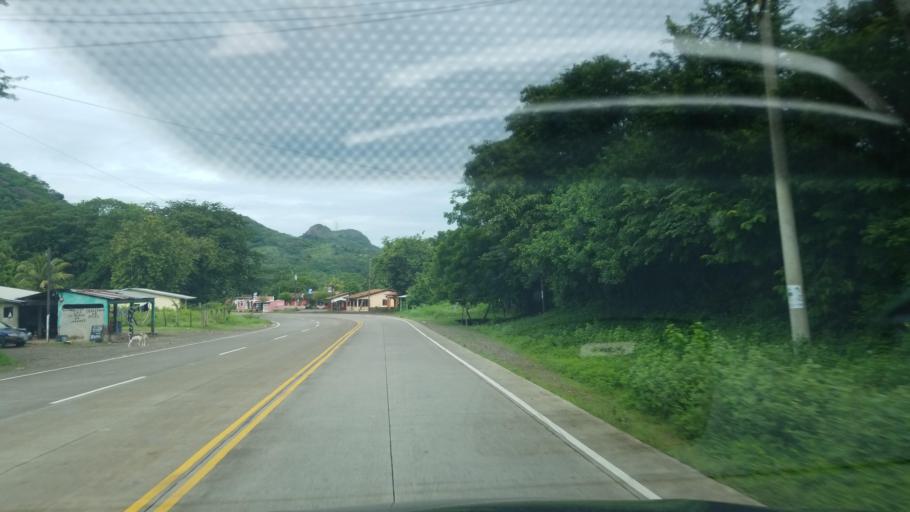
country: HN
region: Francisco Morazan
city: El Porvenir
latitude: 13.6886
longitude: -87.3327
